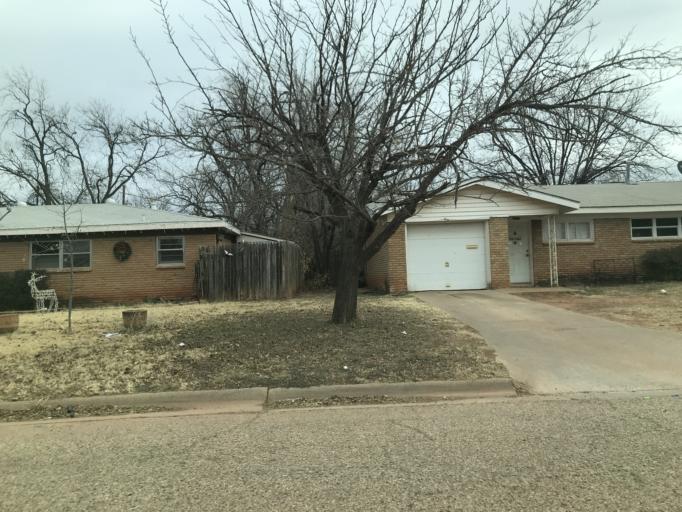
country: US
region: Texas
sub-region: Taylor County
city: Abilene
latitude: 32.4733
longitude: -99.7600
